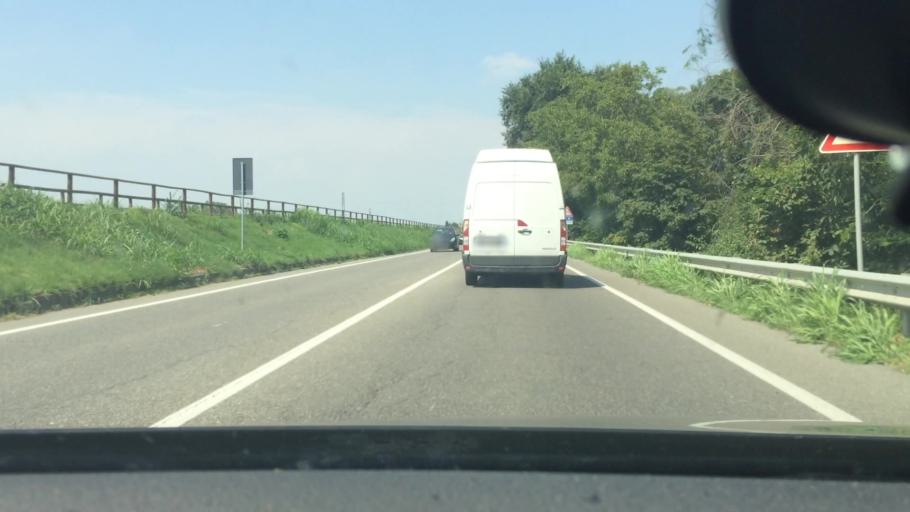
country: IT
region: Lombardy
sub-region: Provincia di Lodi
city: San Rocco al Porto
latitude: 45.0891
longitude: 9.6897
